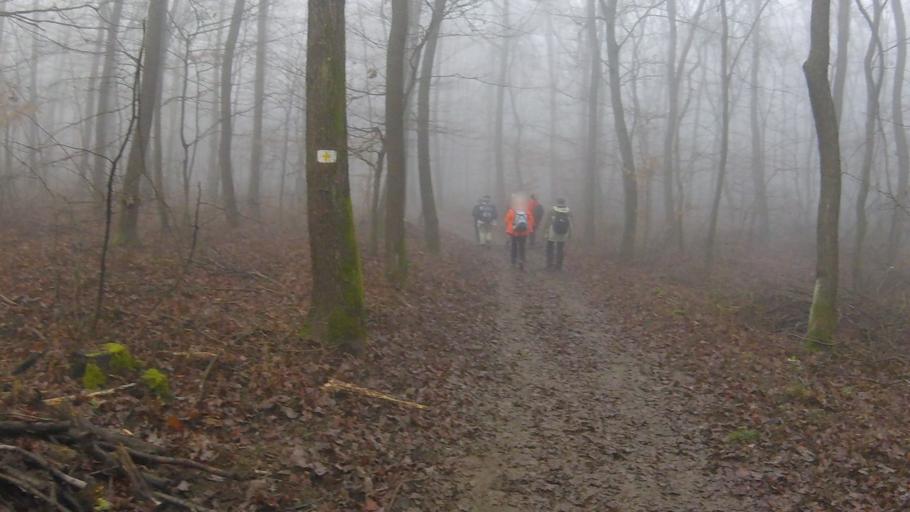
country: HU
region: Pest
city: Budakeszi
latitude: 47.5227
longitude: 18.9476
